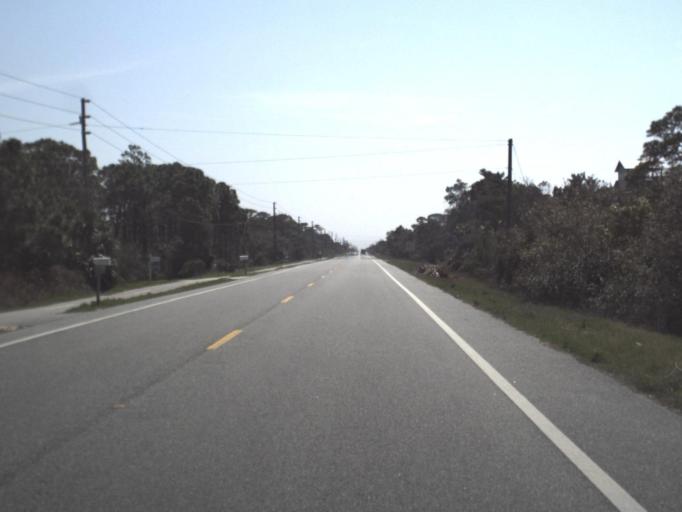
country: US
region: Florida
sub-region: Gulf County
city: Port Saint Joe
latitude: 29.7099
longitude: -85.3807
